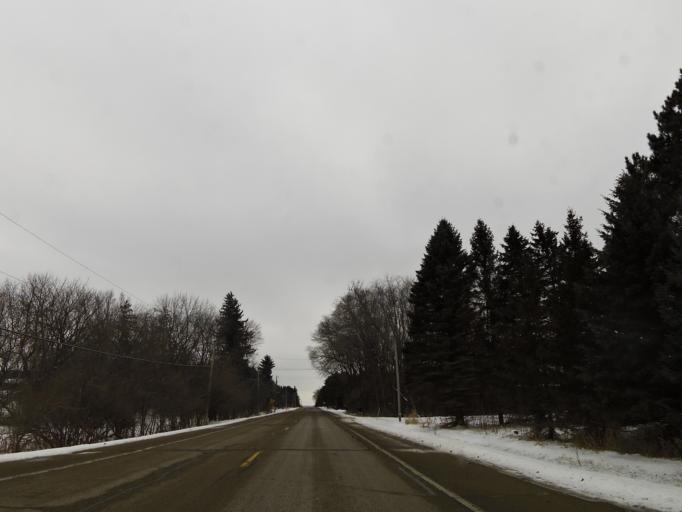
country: US
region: Minnesota
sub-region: Washington County
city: Oak Park Heights
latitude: 44.9857
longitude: -92.8224
